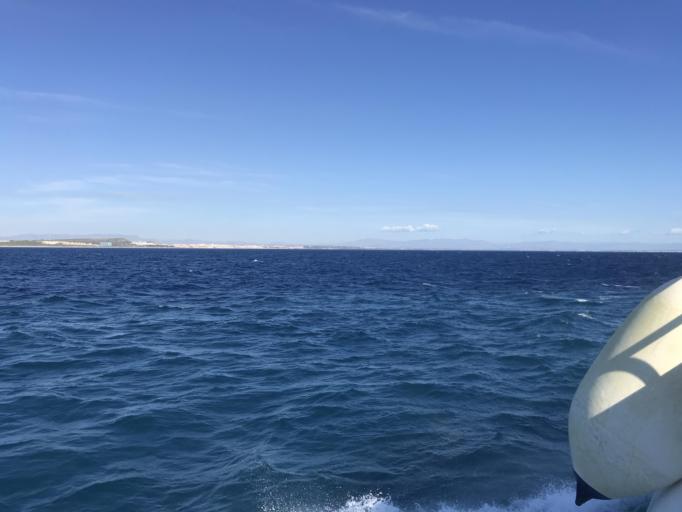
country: ES
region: Valencia
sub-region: Provincia de Alicante
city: Guardamar del Segura
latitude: 38.0284
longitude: -0.6163
